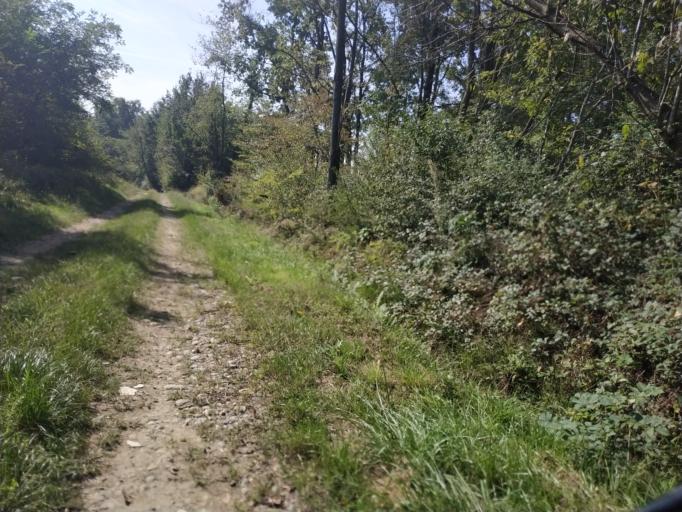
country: IT
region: Piedmont
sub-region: Provincia di Torino
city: Montalenghe
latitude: 45.3252
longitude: 7.8434
